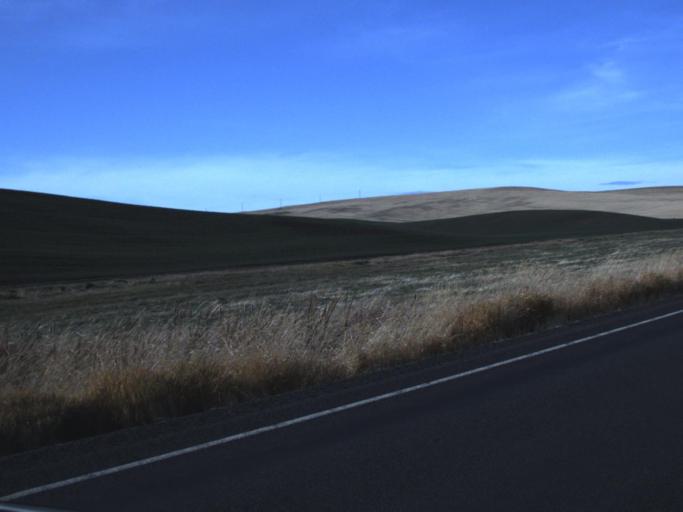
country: US
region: Washington
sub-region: Lincoln County
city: Davenport
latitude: 47.7079
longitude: -118.1464
